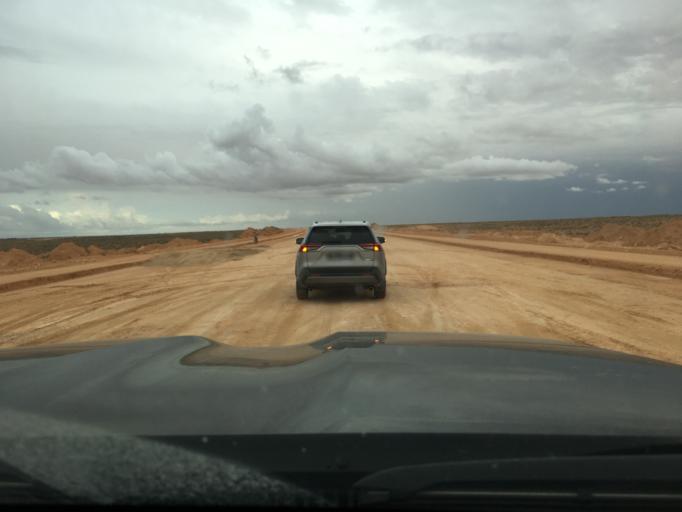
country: TN
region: Madanin
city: Medenine
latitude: 33.2670
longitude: 10.5835
